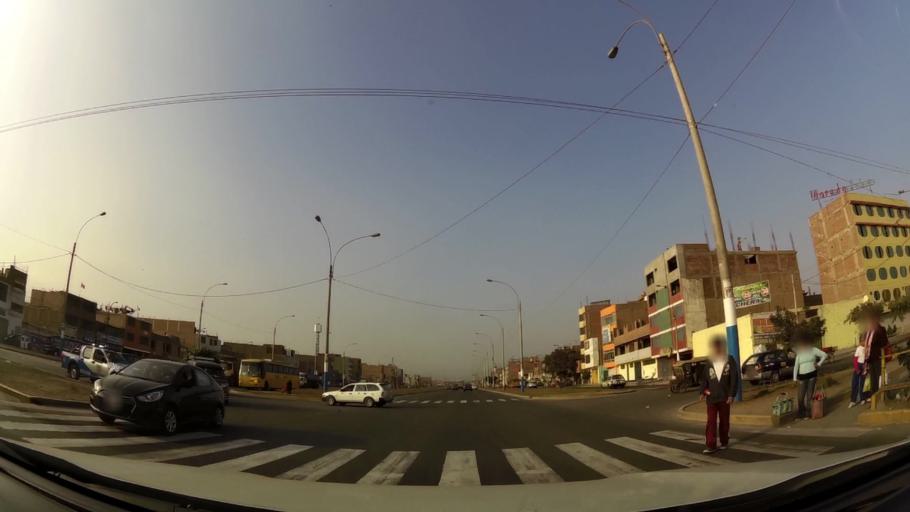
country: PE
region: Lima
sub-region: Lima
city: Independencia
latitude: -11.9780
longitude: -77.0928
